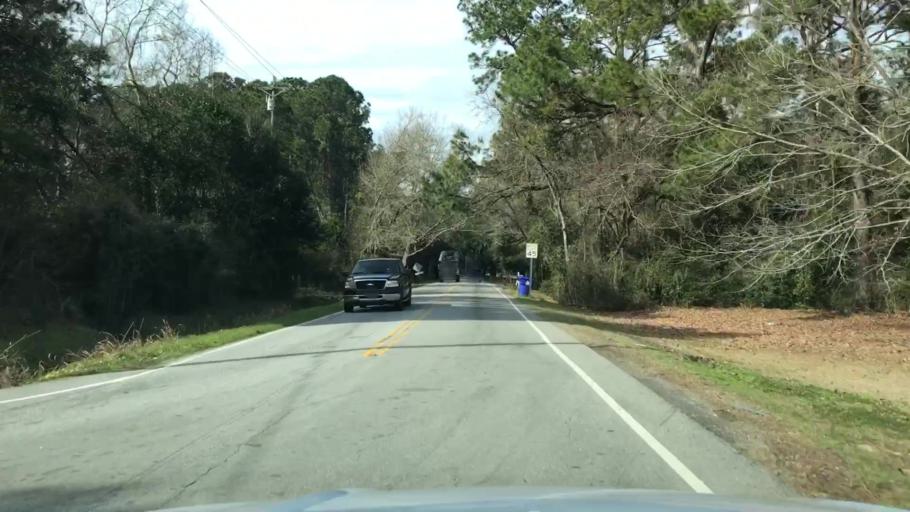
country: US
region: South Carolina
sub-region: Charleston County
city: Shell Point
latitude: 32.7676
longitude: -80.0708
